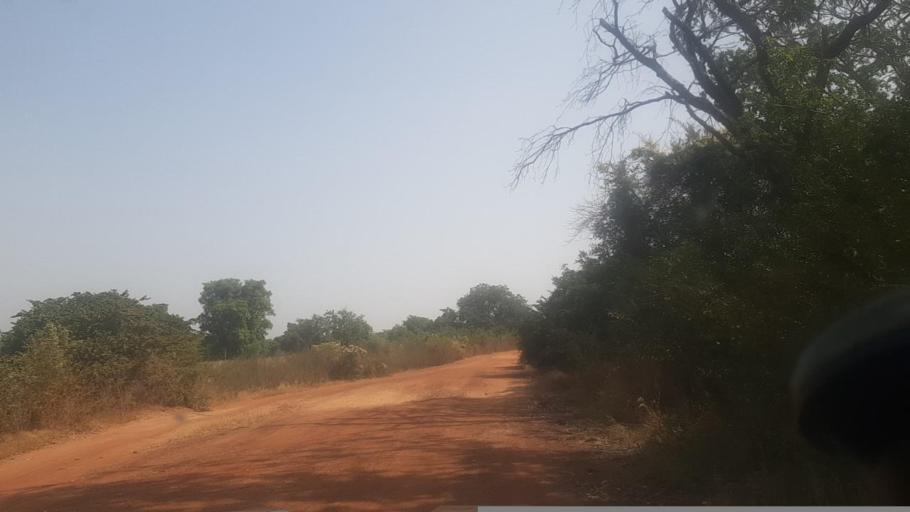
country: ML
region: Segou
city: Bla
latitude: 12.9209
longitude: -6.2595
